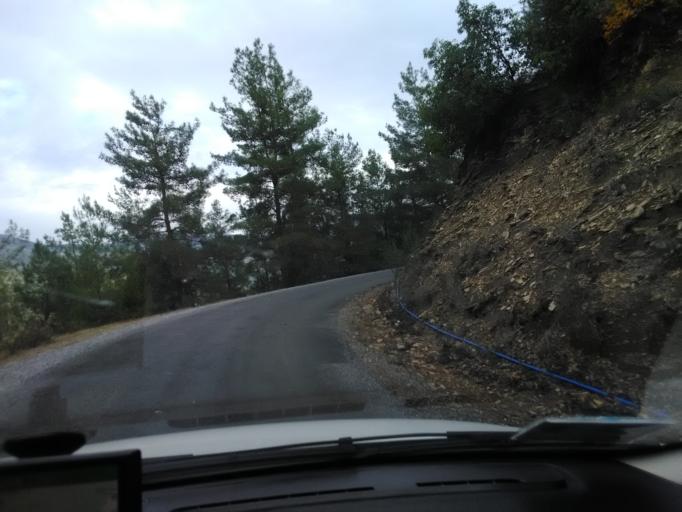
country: TR
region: Antalya
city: Gazipasa
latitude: 36.2454
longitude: 32.4326
